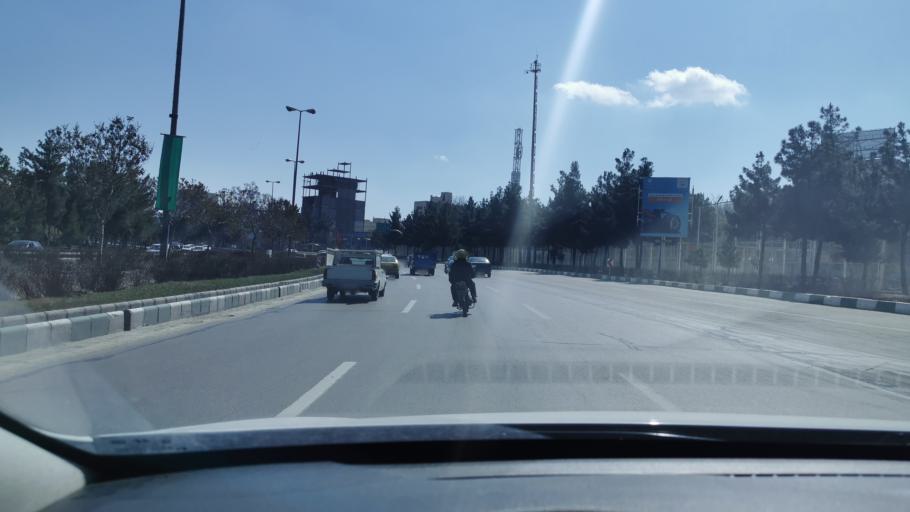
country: IR
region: Razavi Khorasan
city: Mashhad
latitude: 36.3023
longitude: 59.5372
